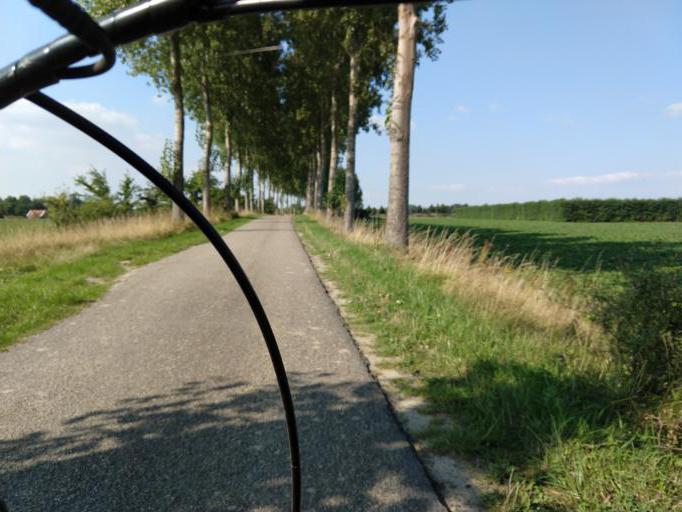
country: NL
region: Zeeland
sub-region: Gemeente Goes
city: Goes
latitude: 51.4276
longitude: 3.8413
